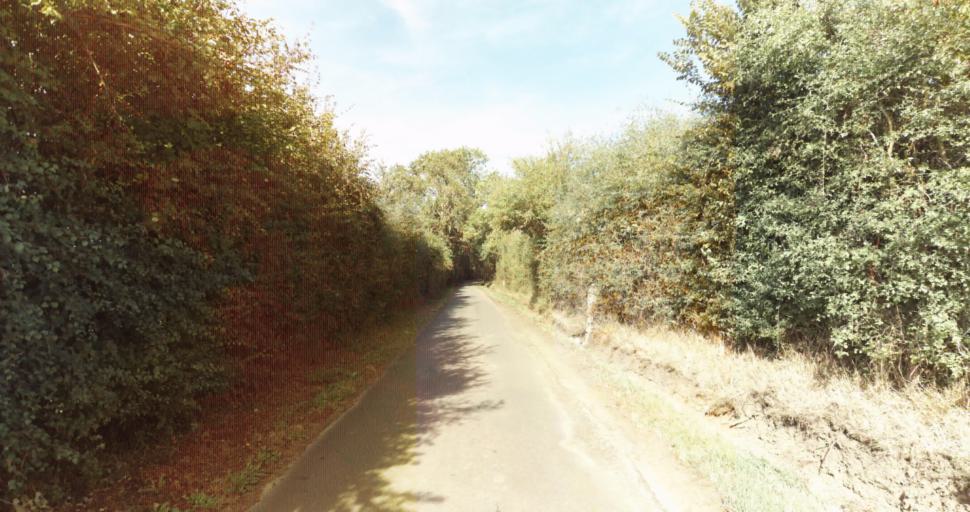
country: FR
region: Lower Normandy
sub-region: Departement de l'Orne
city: Gace
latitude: 48.7105
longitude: 0.2201
